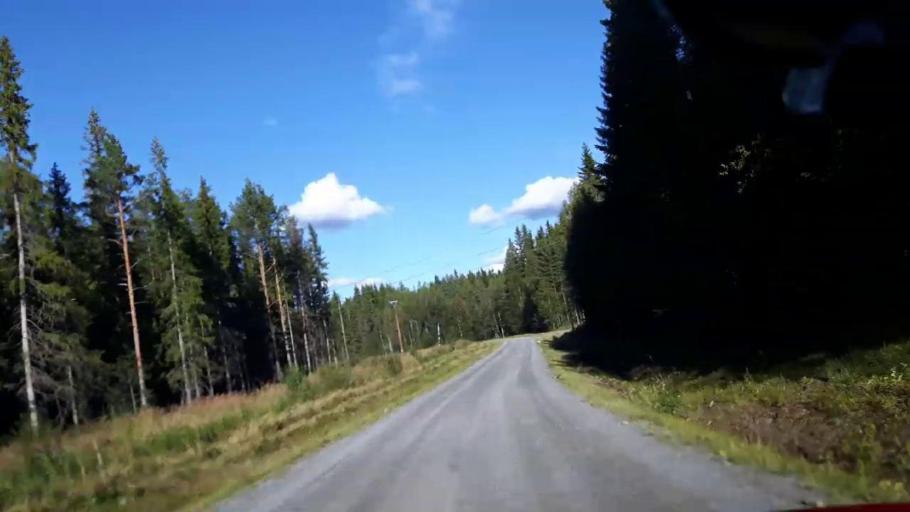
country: SE
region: Jaemtland
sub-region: Ragunda Kommun
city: Hammarstrand
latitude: 63.5139
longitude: 16.0517
